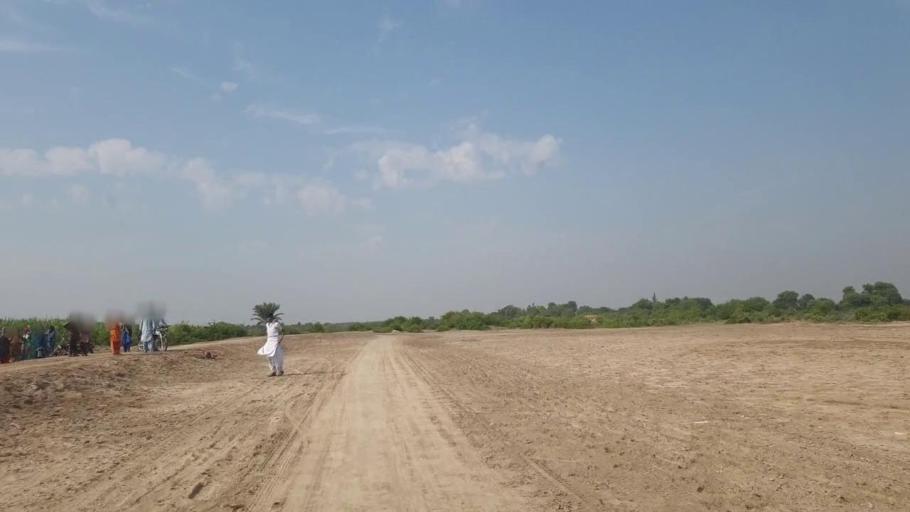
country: PK
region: Sindh
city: Digri
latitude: 25.0331
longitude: 69.0693
